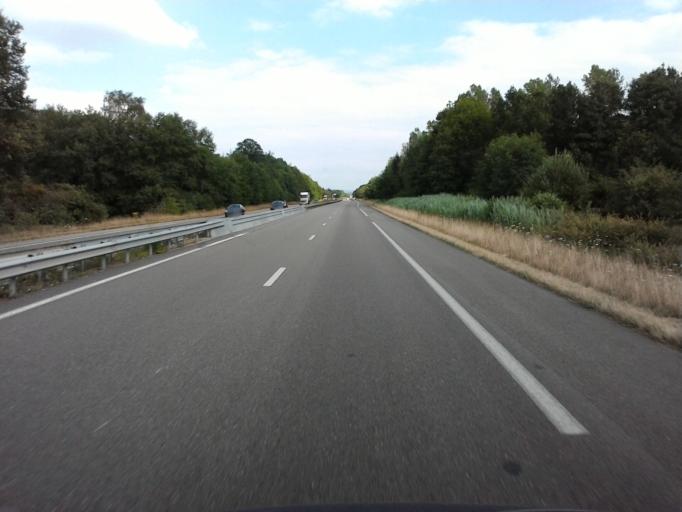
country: FR
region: Lorraine
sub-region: Departement des Vosges
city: Thaon-les-Vosges
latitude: 48.2445
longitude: 6.4067
